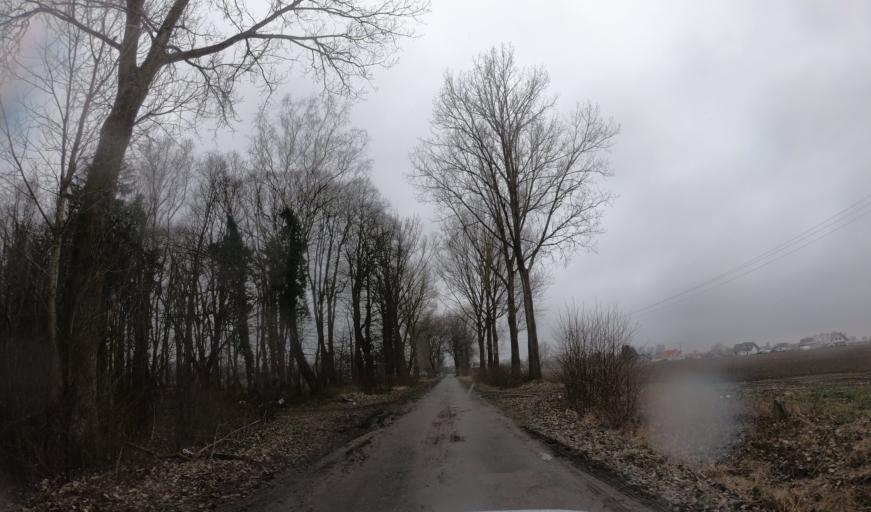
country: PL
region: West Pomeranian Voivodeship
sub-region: Powiat kamienski
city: Kamien Pomorski
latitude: 53.9045
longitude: 14.8307
